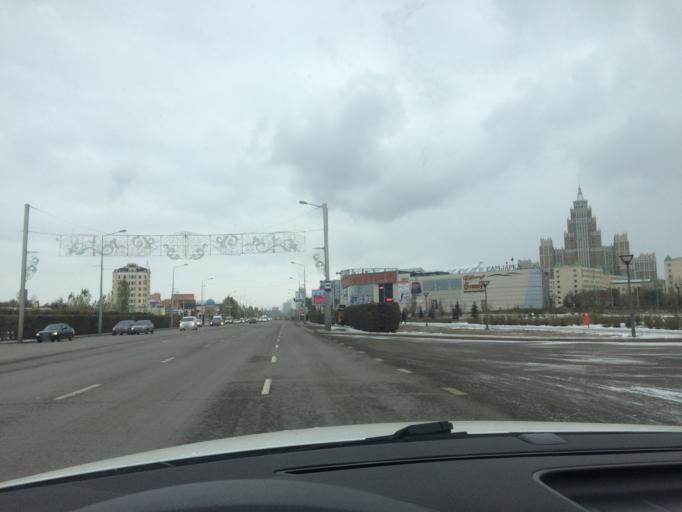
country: KZ
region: Astana Qalasy
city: Astana
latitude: 51.1355
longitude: 71.4081
